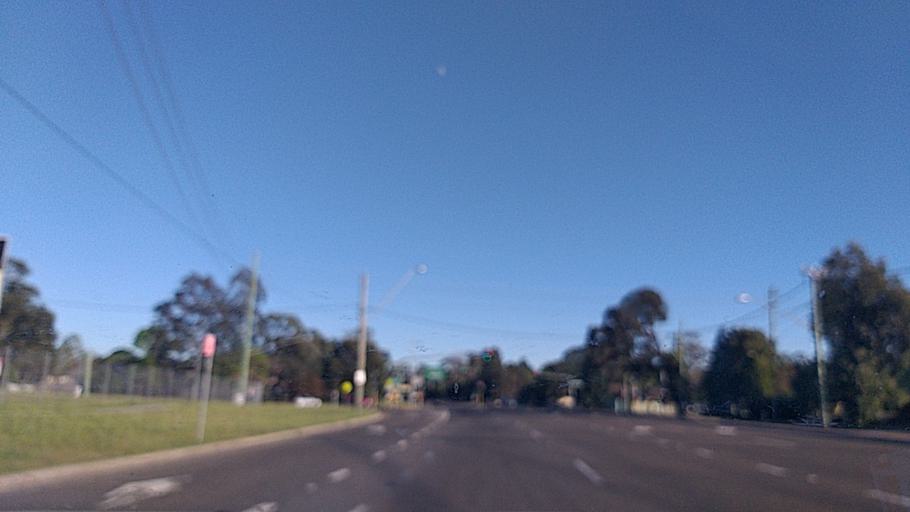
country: AU
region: New South Wales
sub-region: Bankstown
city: Milperra
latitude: -33.9462
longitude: 150.9472
